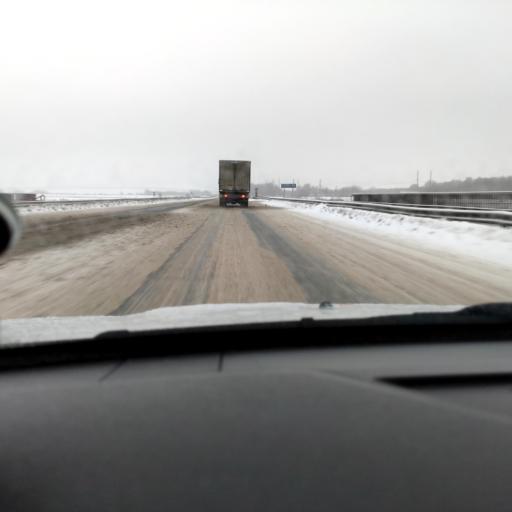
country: RU
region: Samara
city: Smyshlyayevka
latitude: 53.2611
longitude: 50.4736
